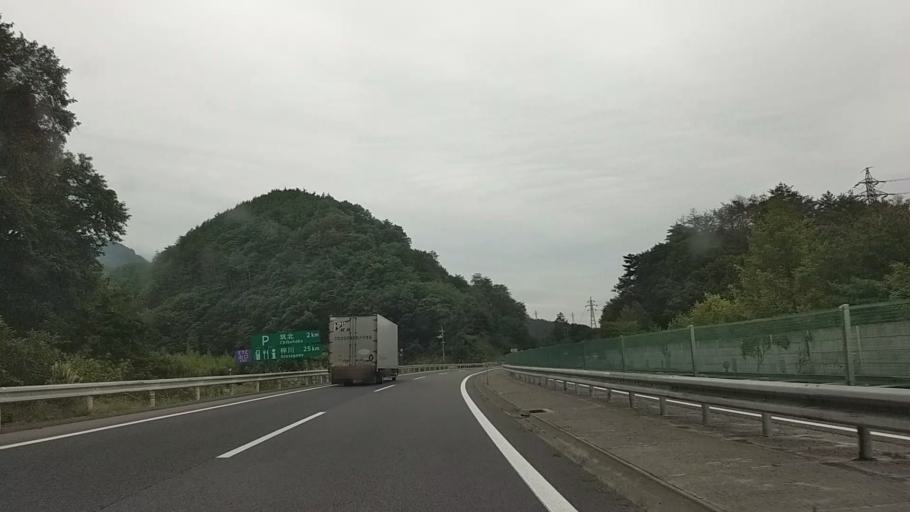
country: JP
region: Nagano
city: Omachi
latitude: 36.4481
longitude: 138.0445
